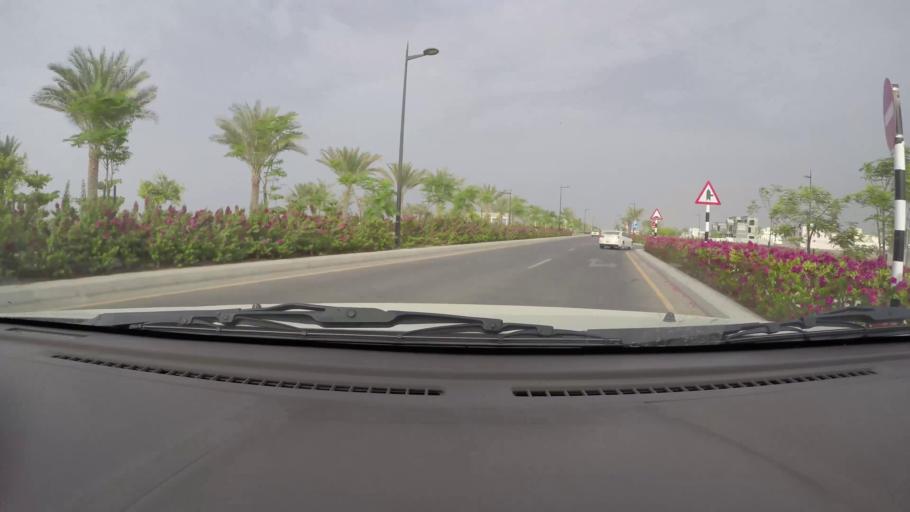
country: OM
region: Muhafazat Masqat
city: As Sib al Jadidah
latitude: 23.6939
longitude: 58.1602
